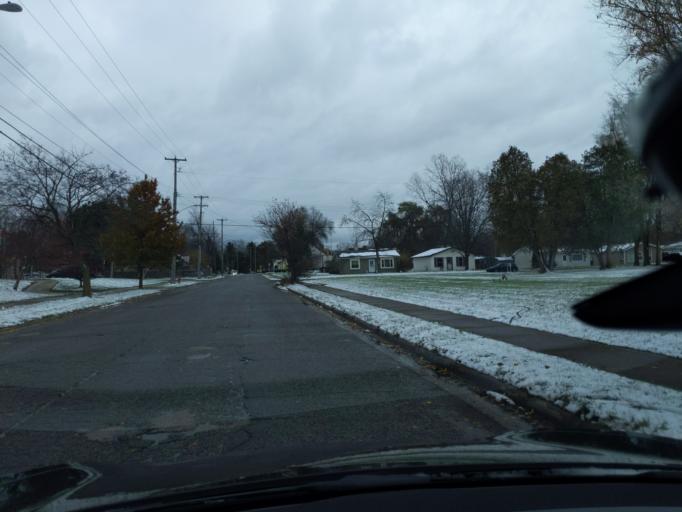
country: US
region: Michigan
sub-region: Ingham County
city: Lansing
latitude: 42.6867
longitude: -84.5845
